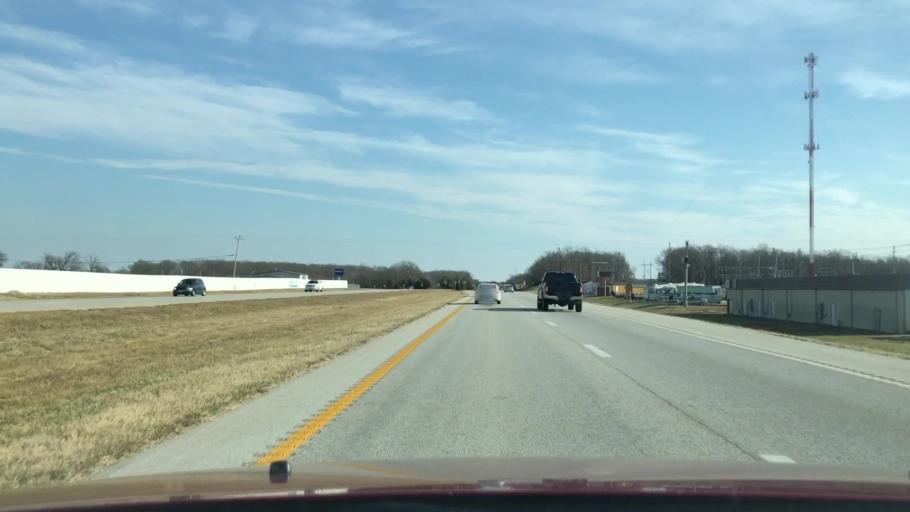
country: US
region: Missouri
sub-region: Webster County
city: Rogersville
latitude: 37.1180
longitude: -93.0169
